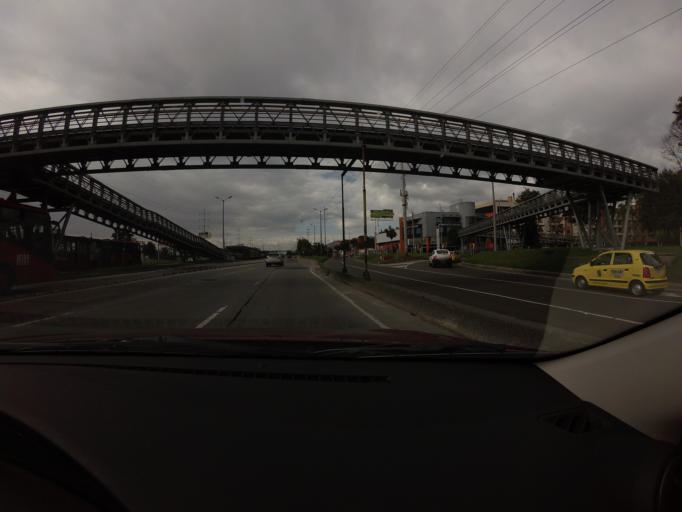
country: CO
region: Bogota D.C.
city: Barrio San Luis
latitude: 4.7195
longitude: -74.0516
